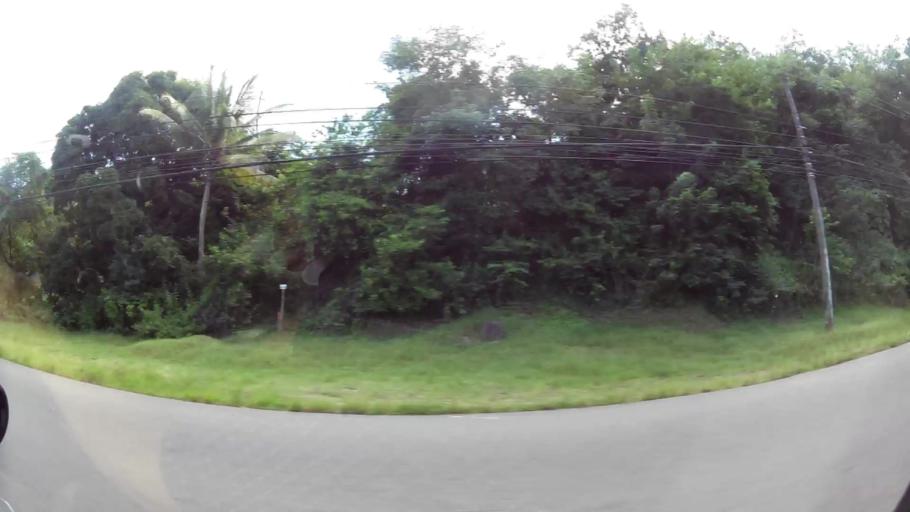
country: TT
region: Tobago
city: Scarborough
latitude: 11.2039
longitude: -60.7824
